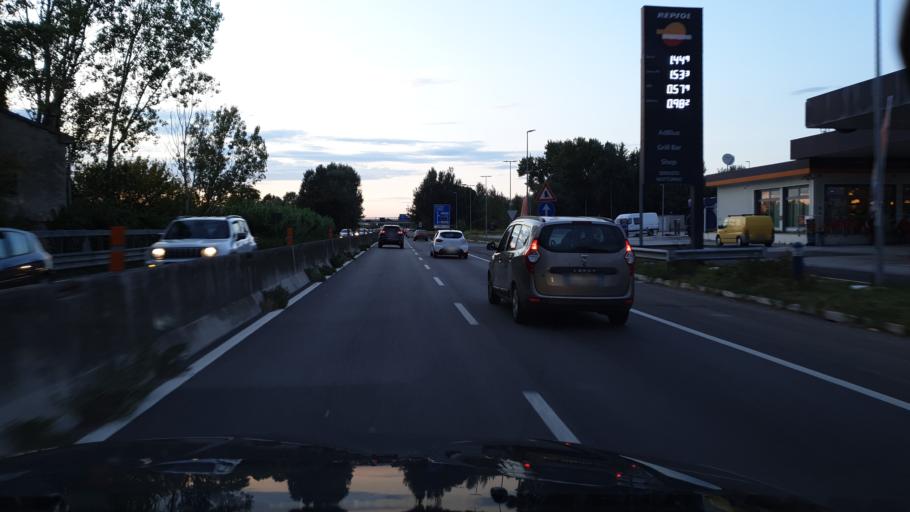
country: IT
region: Emilia-Romagna
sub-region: Provincia di Ravenna
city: Ravenna
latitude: 44.4070
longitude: 12.1753
